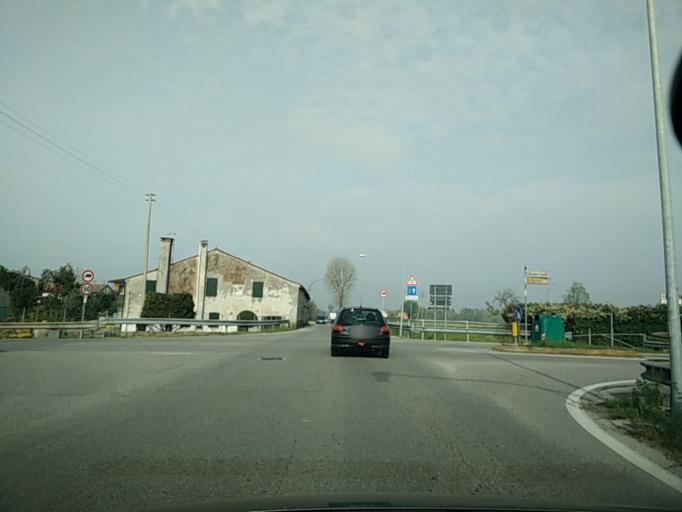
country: IT
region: Veneto
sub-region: Provincia di Venezia
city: Ballo
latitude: 45.4743
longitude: 12.0564
